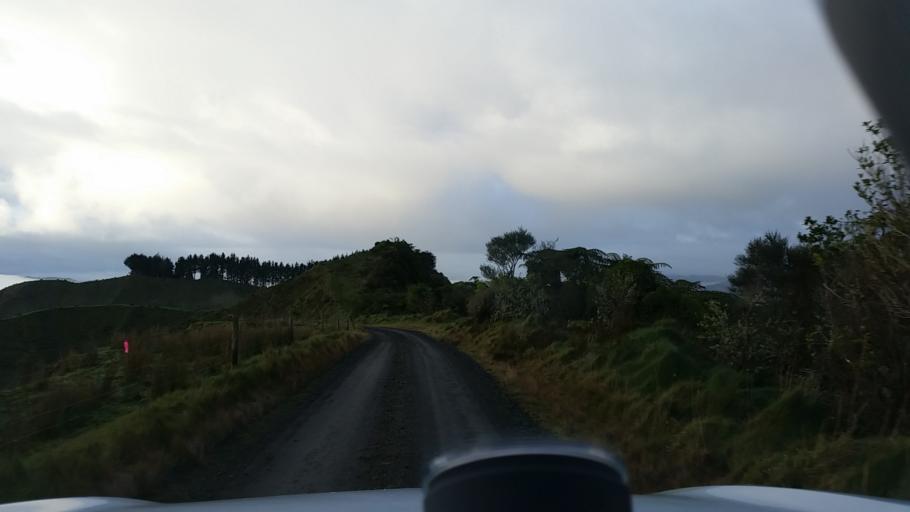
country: NZ
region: Taranaki
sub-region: South Taranaki District
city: Eltham
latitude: -39.4442
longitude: 174.4518
